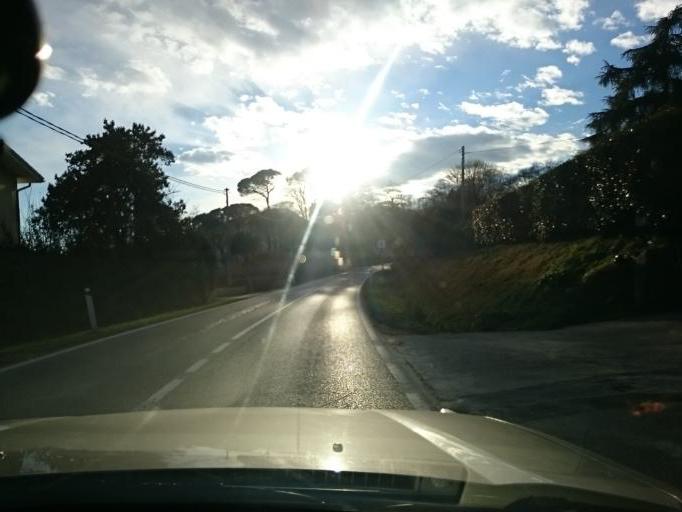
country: IT
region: Veneto
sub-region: Provincia di Padova
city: Torreglia
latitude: 45.3429
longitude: 11.7375
